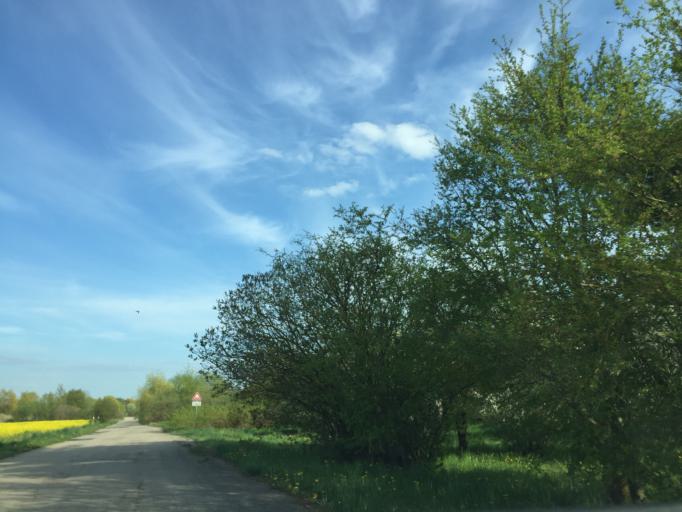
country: LV
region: Bauskas Rajons
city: Bauska
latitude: 56.3248
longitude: 24.2637
